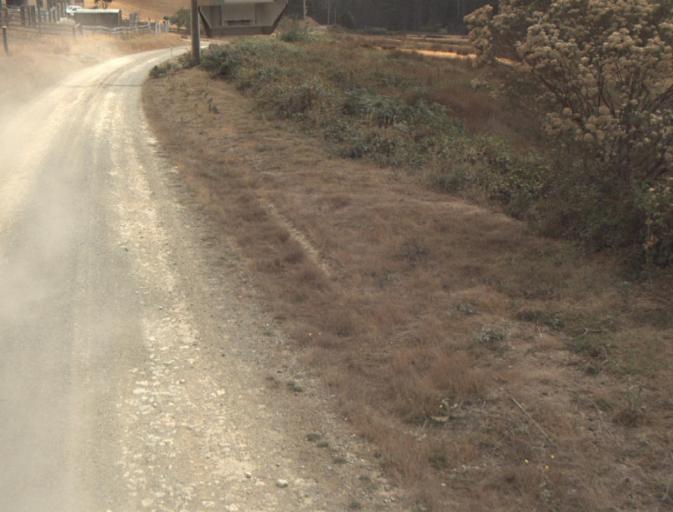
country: AU
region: Tasmania
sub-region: Dorset
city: Bridport
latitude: -41.1894
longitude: 147.2617
